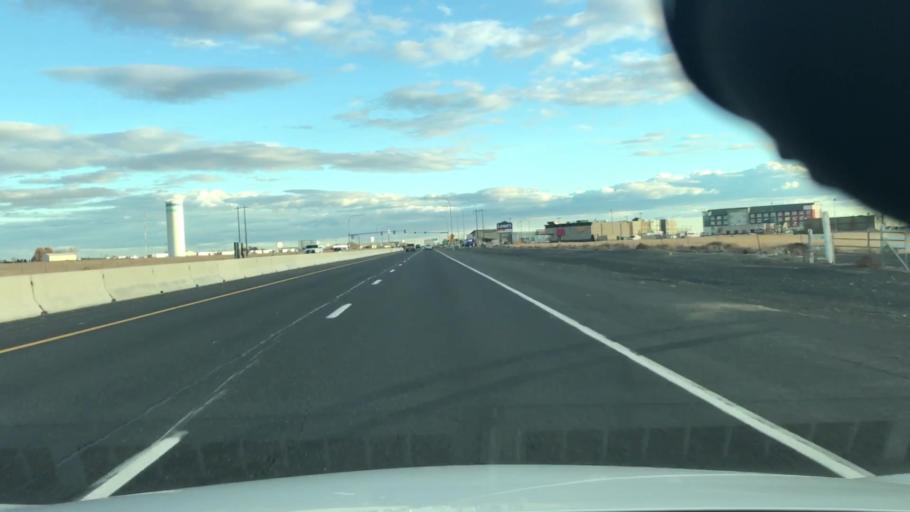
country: US
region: Washington
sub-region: Grant County
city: Moses Lake
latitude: 47.1083
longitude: -119.2546
